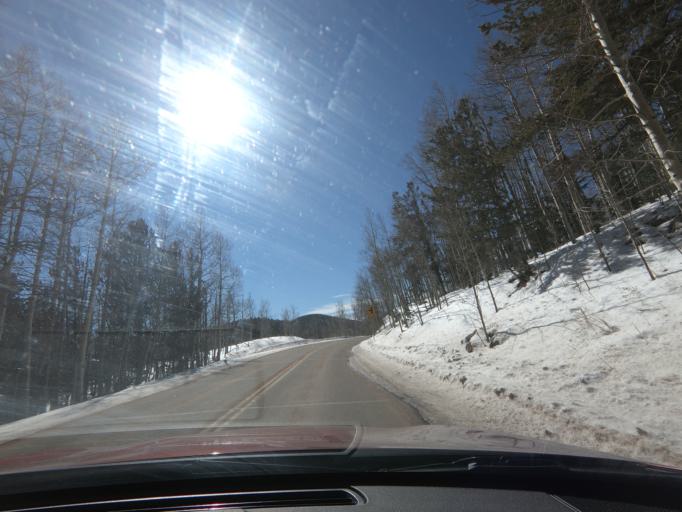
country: US
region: Colorado
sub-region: Teller County
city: Cripple Creek
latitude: 38.7453
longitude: -105.1001
